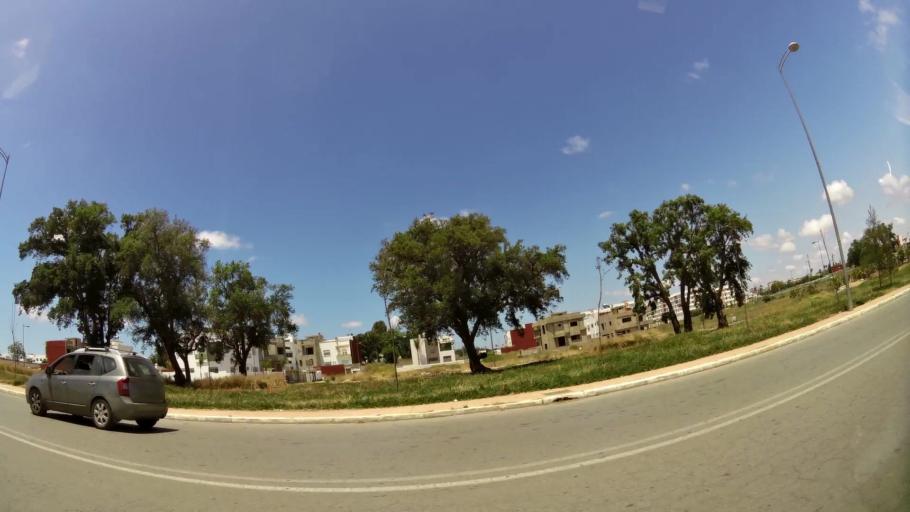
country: MA
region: Gharb-Chrarda-Beni Hssen
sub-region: Kenitra Province
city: Kenitra
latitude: 34.2488
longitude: -6.5641
